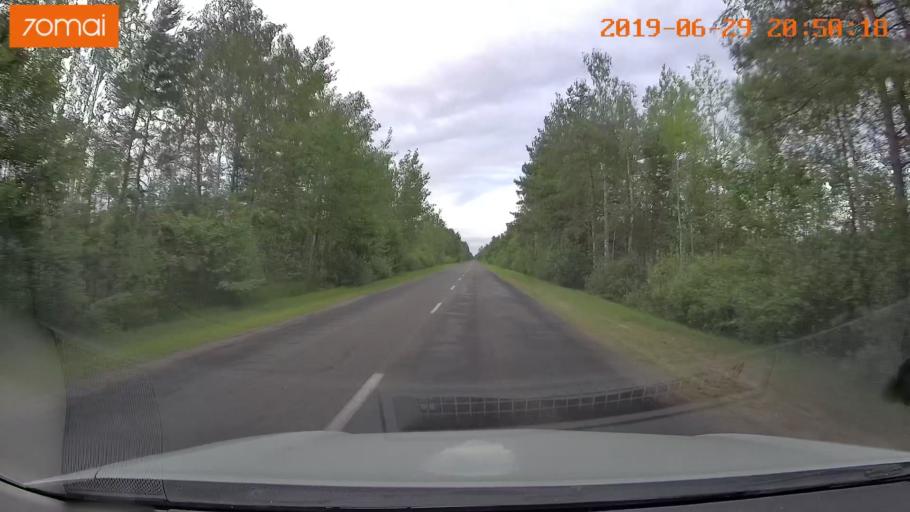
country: BY
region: Brest
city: Hantsavichy
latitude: 52.6750
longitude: 26.3341
